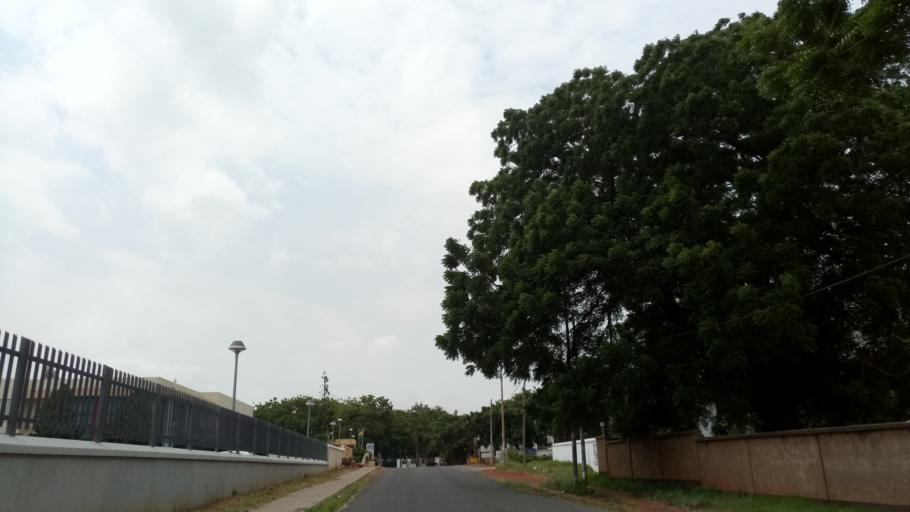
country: GH
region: Greater Accra
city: Accra
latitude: 5.5587
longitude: -0.1923
